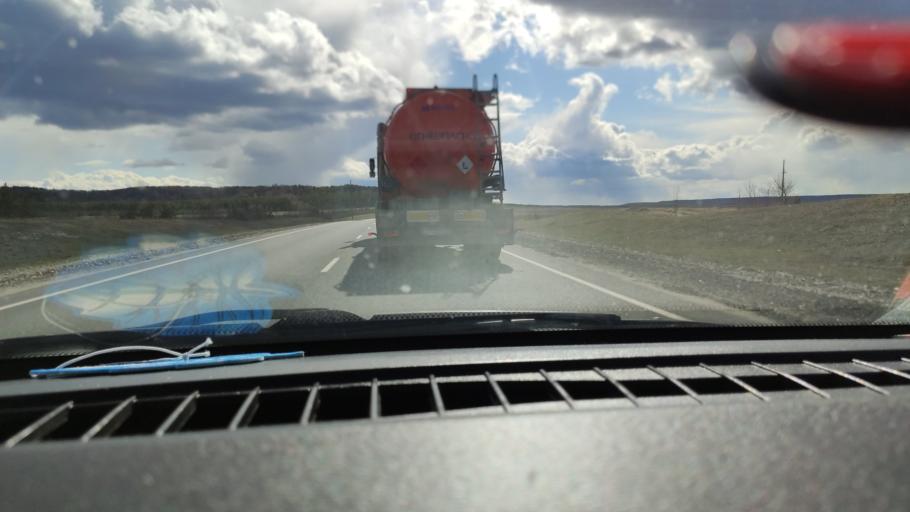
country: RU
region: Saratov
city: Khvalynsk
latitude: 52.5470
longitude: 48.0691
